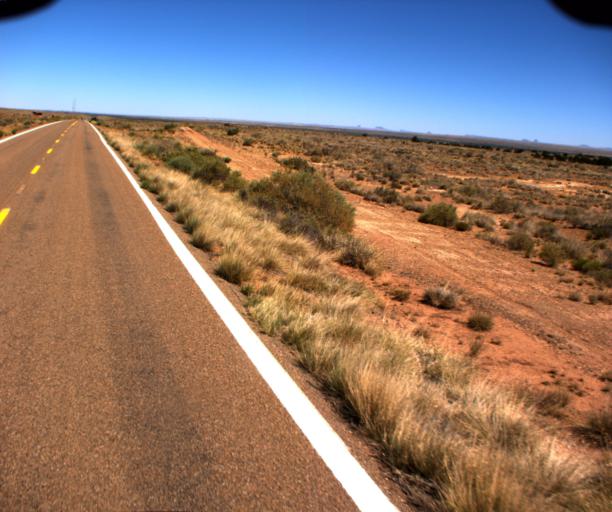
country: US
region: Arizona
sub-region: Navajo County
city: Winslow
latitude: 34.9432
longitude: -110.6445
